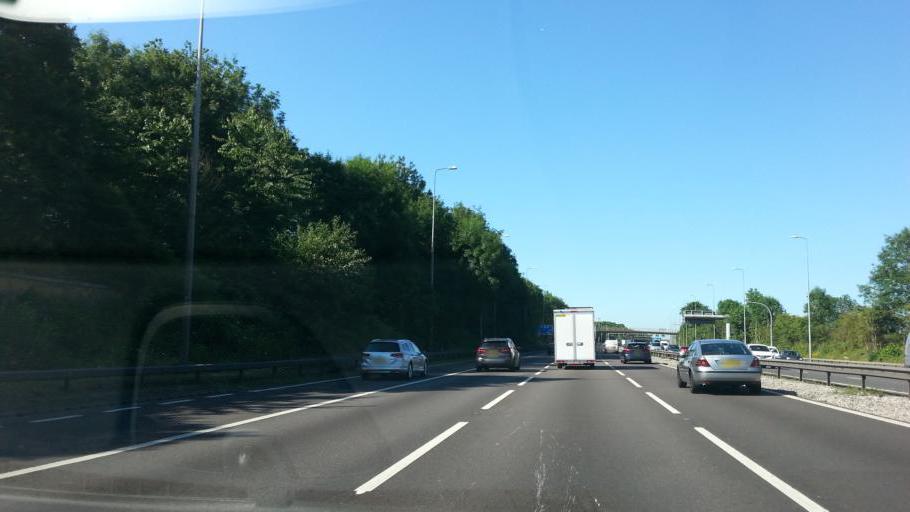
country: GB
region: England
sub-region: Solihull
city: Solihull
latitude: 52.3975
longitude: -1.7631
